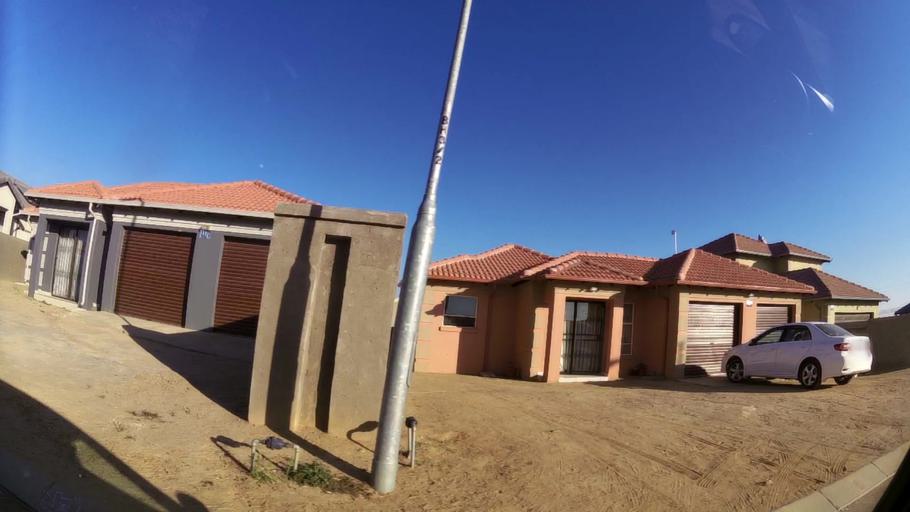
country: ZA
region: Gauteng
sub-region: City of Johannesburg Metropolitan Municipality
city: Midrand
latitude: -25.9271
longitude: 28.1002
